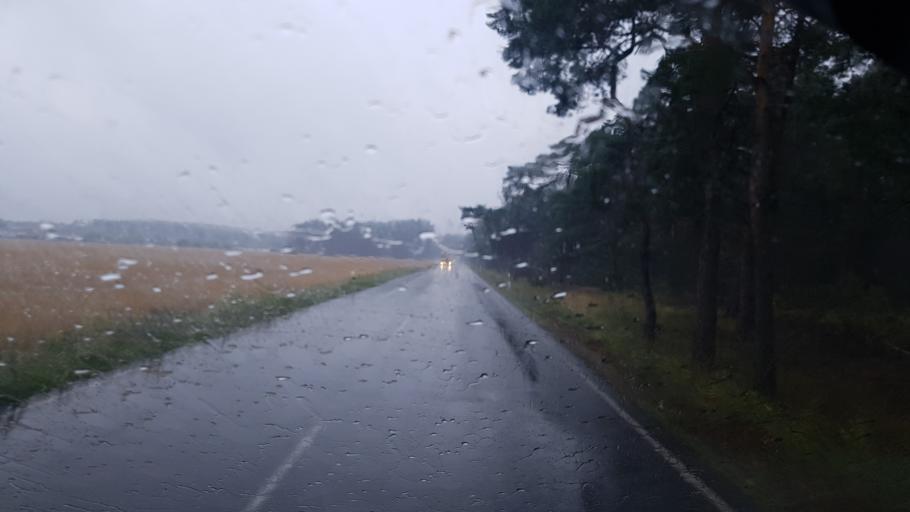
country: DE
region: Brandenburg
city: Baruth
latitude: 52.0569
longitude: 13.5622
